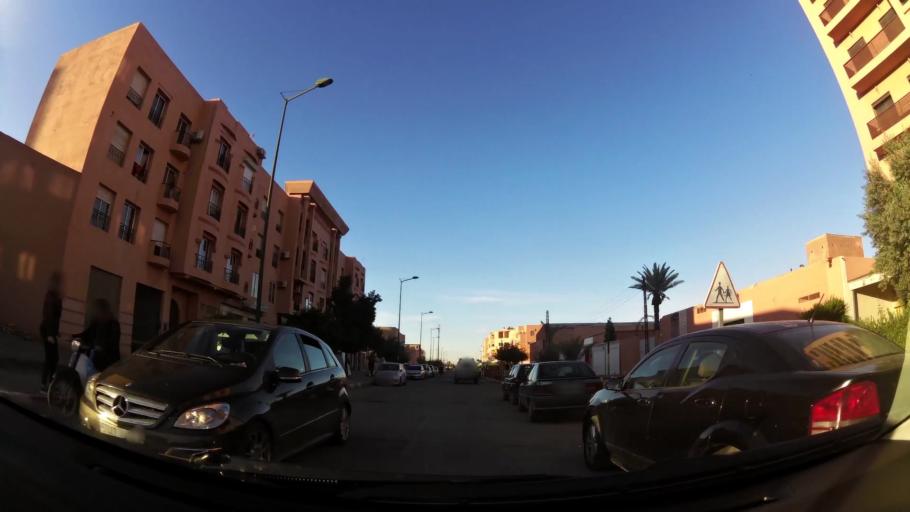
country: MA
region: Marrakech-Tensift-Al Haouz
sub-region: Marrakech
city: Marrakesh
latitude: 31.6243
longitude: -8.0295
